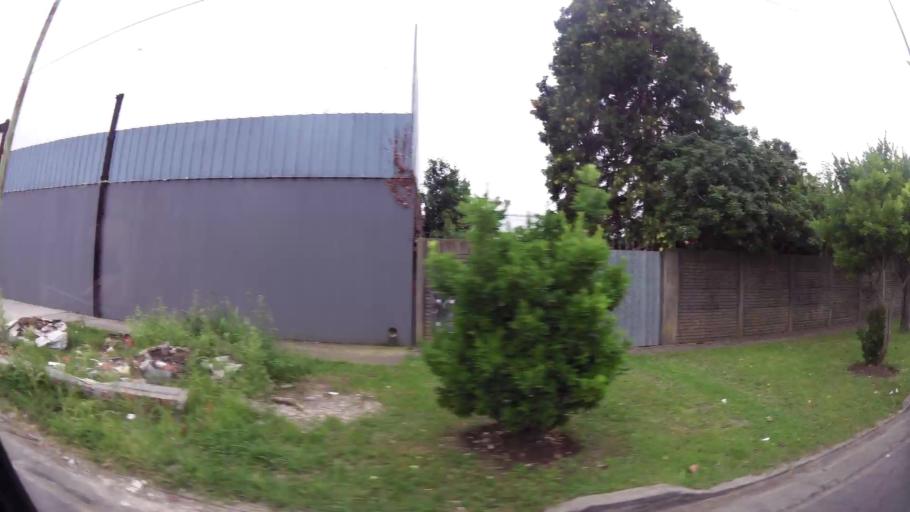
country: AR
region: Buenos Aires
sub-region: Partido de La Plata
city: La Plata
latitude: -34.9310
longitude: -57.9862
